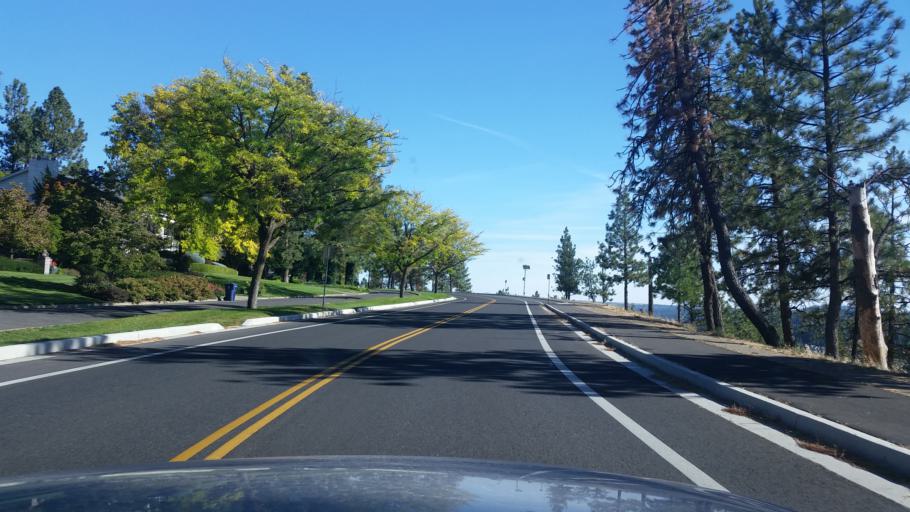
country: US
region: Washington
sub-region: Spokane County
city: Spokane
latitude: 47.6212
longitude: -117.4260
